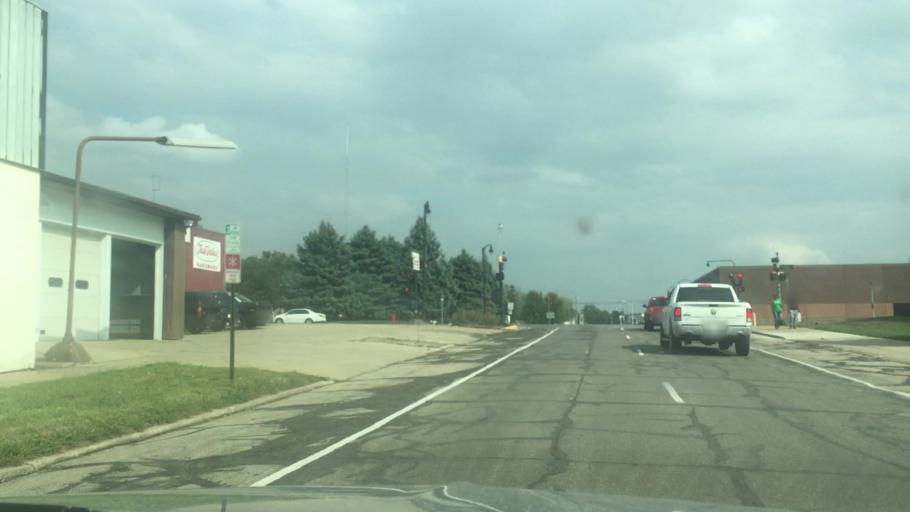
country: US
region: Iowa
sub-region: Marshall County
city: Marshalltown
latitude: 42.0467
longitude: -92.9137
